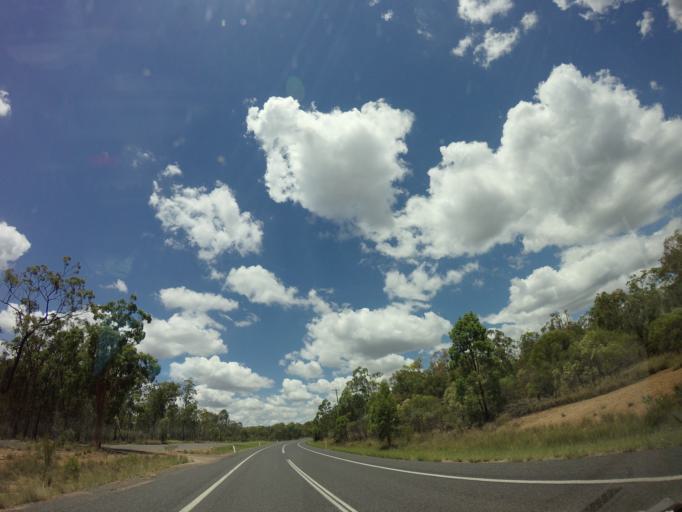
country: AU
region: Queensland
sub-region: Western Downs
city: Dalby
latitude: -27.9669
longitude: 151.0049
